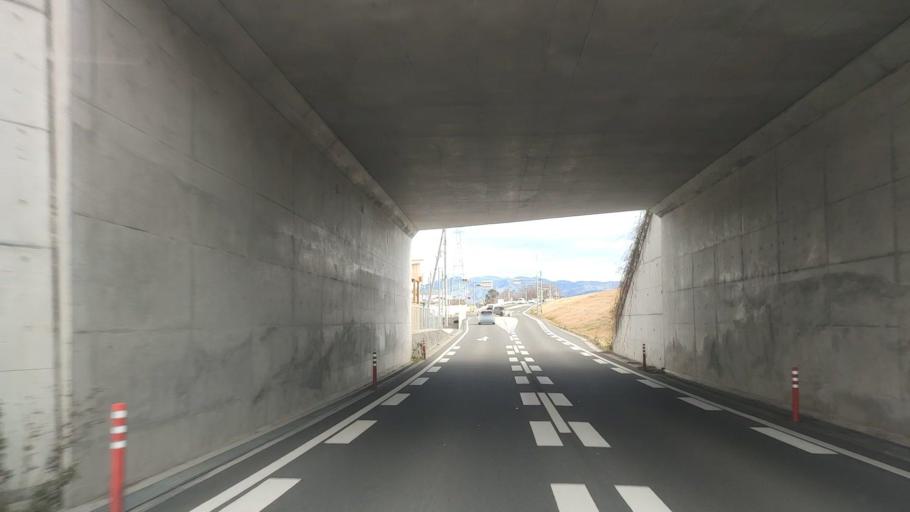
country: JP
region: Ehime
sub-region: Shikoku-chuo Shi
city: Matsuyama
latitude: 33.8147
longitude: 132.7494
